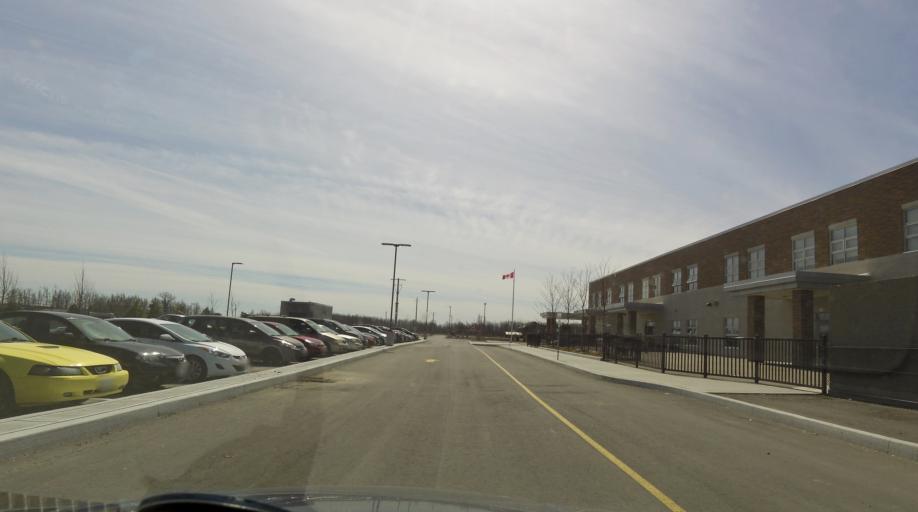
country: CA
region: Ontario
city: Brampton
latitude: 43.7024
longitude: -79.8728
